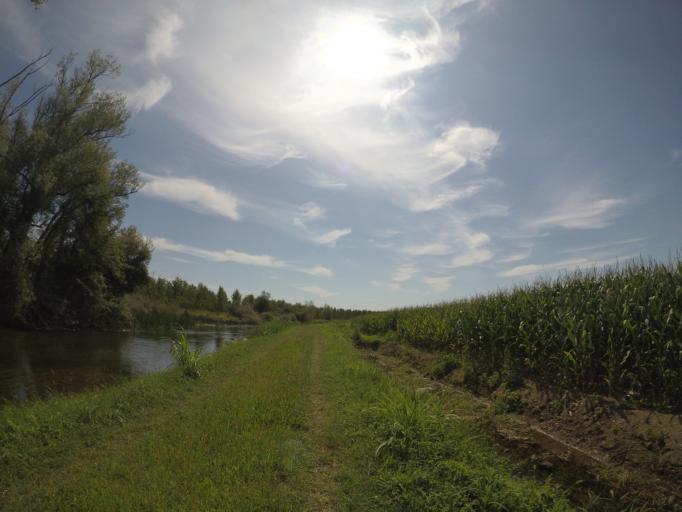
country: IT
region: Friuli Venezia Giulia
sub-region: Provincia di Udine
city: Bertiolo
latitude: 45.9209
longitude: 13.0198
